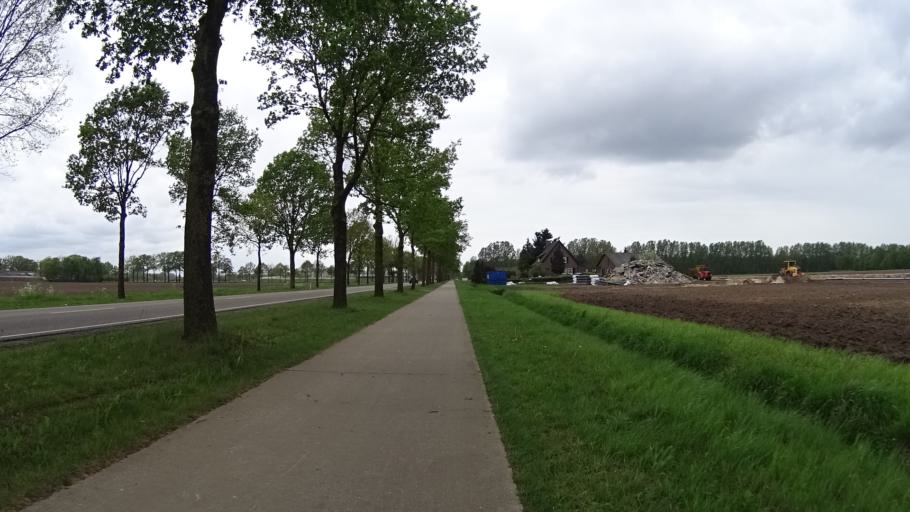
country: NL
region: North Brabant
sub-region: Gemeente Veghel
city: Keldonk
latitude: 51.6042
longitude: 5.5872
